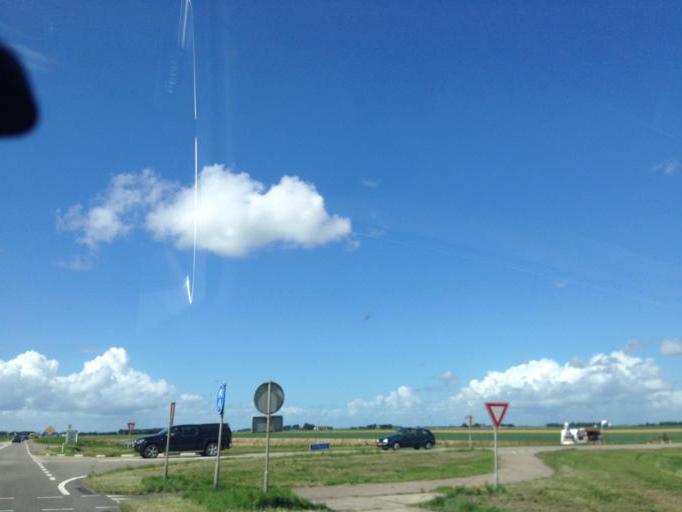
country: NL
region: Flevoland
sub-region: Gemeente Dronten
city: Dronten
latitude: 52.5467
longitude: 5.7059
